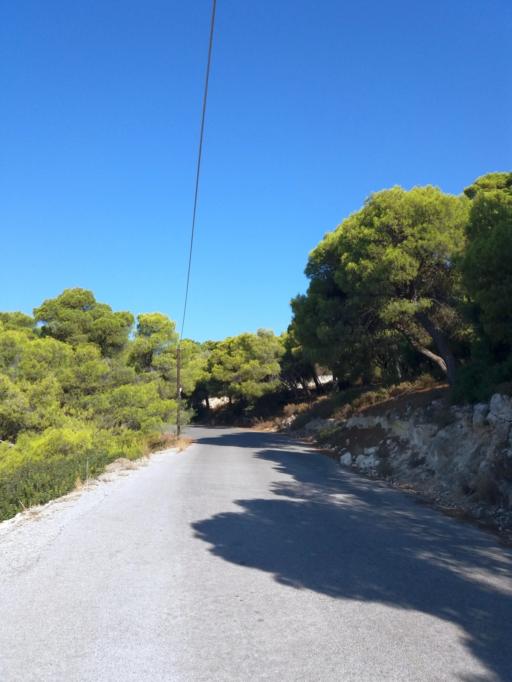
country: GR
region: Attica
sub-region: Nomos Piraios
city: Vathi
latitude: 37.7531
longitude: 23.5354
